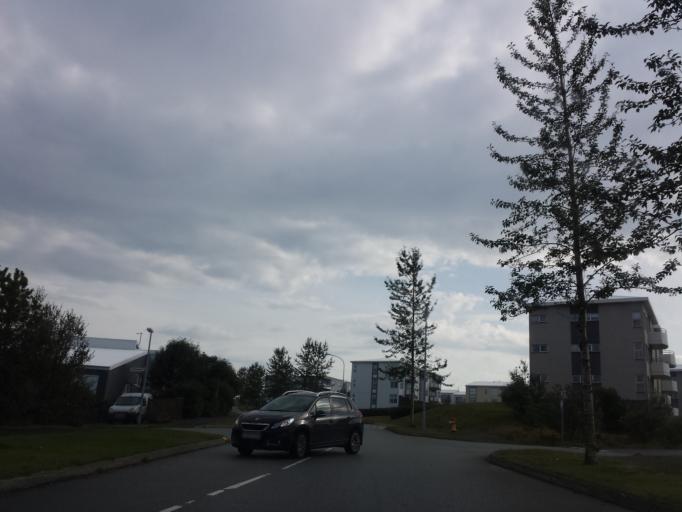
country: IS
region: Capital Region
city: Kopavogur
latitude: 64.0998
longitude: -21.9030
